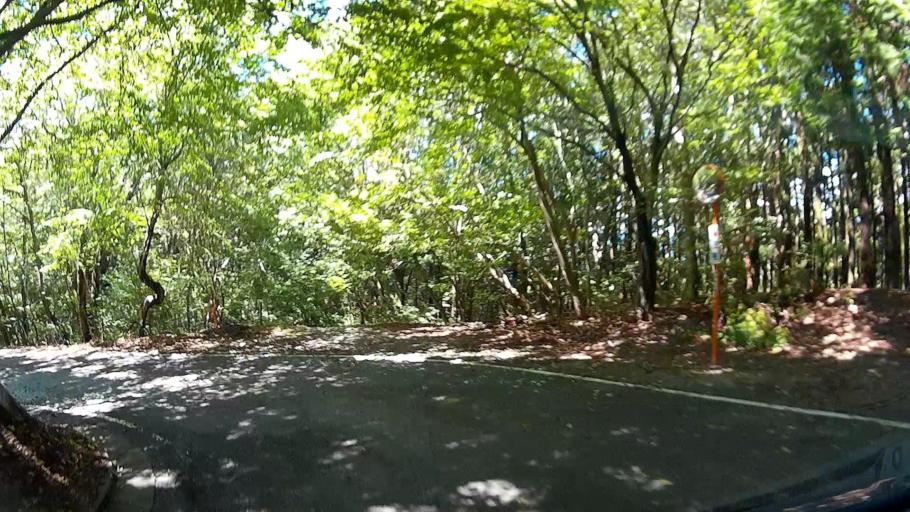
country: JP
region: Shizuoka
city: Shizuoka-shi
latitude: 35.2055
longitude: 138.2625
